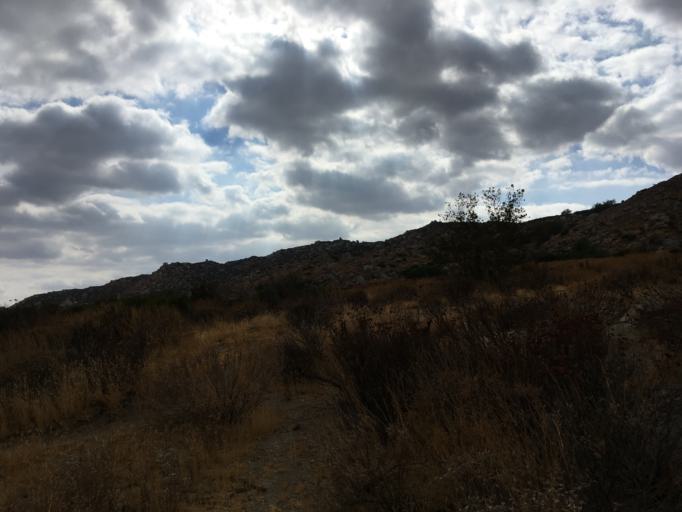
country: US
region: California
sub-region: Riverside County
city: Green Acres
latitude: 33.7813
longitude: -117.0545
